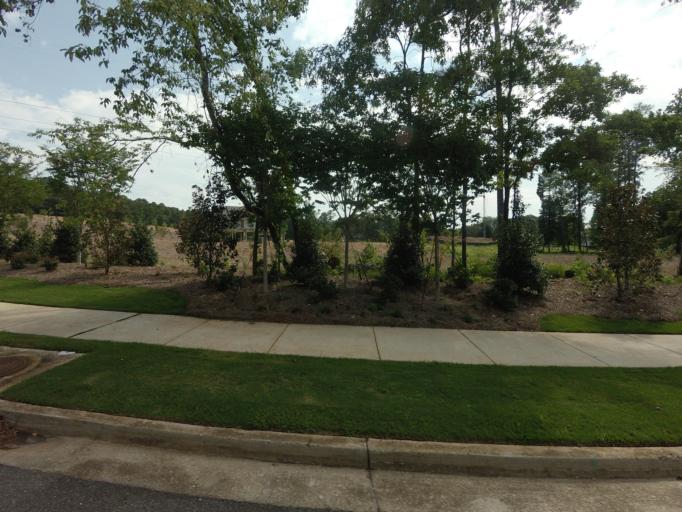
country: US
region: Georgia
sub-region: Fulton County
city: Johns Creek
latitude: 34.0479
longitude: -84.2389
